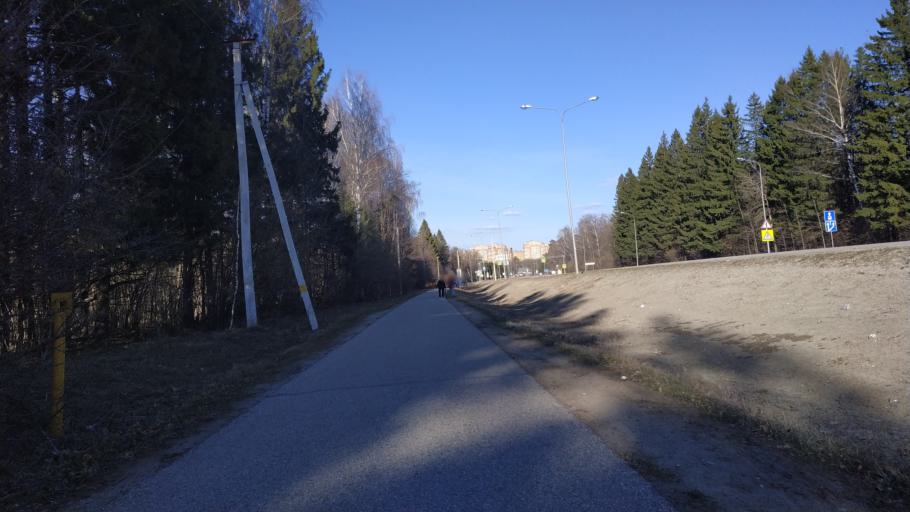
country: RU
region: Chuvashia
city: Novyye Lapsary
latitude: 56.1297
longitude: 47.1339
